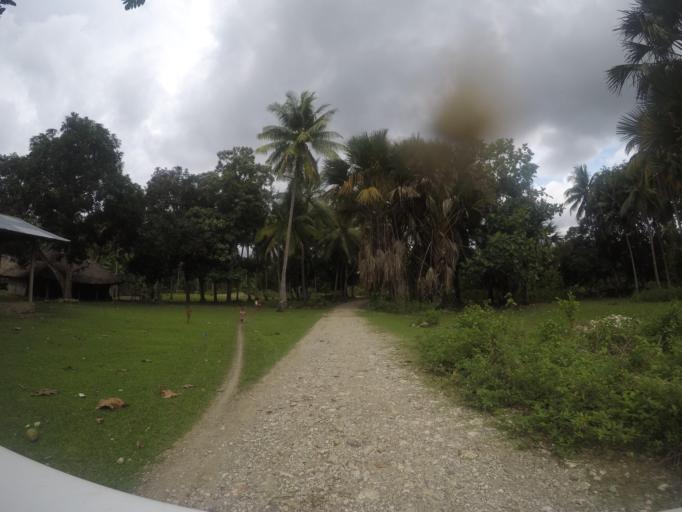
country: TL
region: Viqueque
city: Viqueque
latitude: -8.8536
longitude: 126.3542
